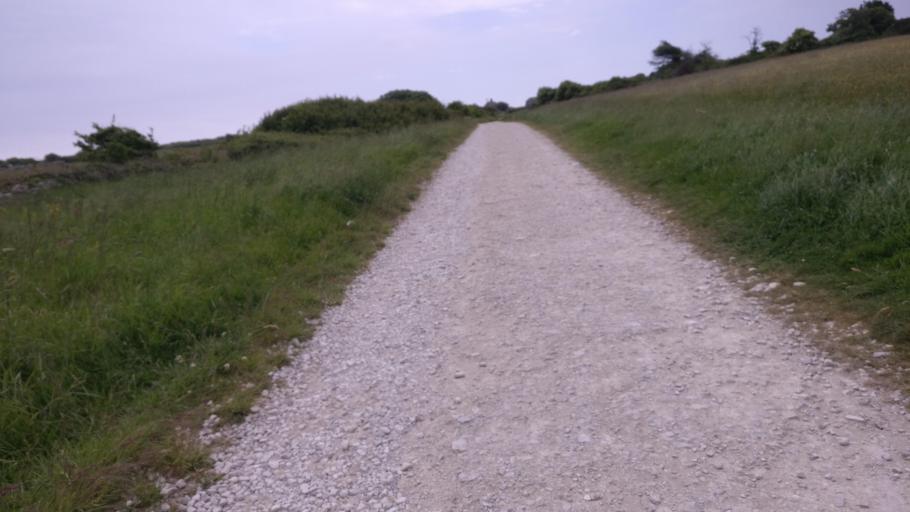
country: GB
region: England
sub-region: Dorset
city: Swanage
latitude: 50.6024
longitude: -2.0039
